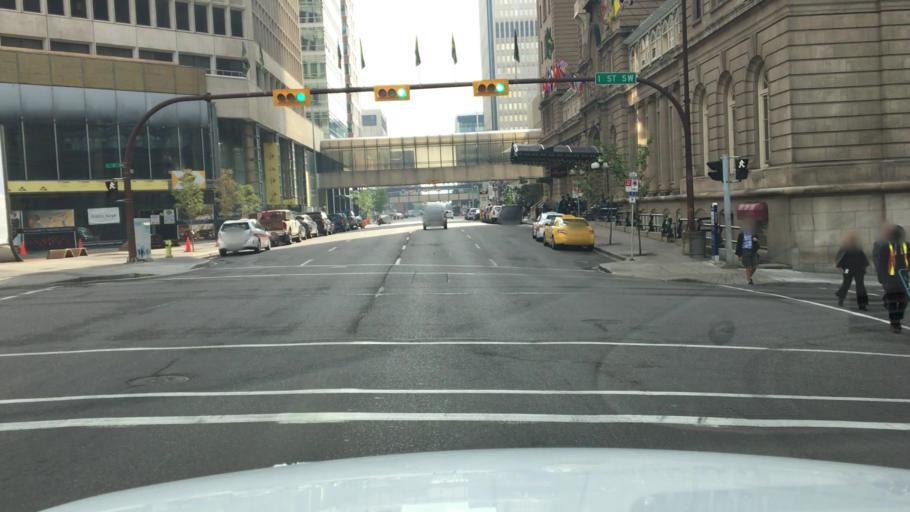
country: CA
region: Alberta
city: Calgary
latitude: 51.0446
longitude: -114.0657
